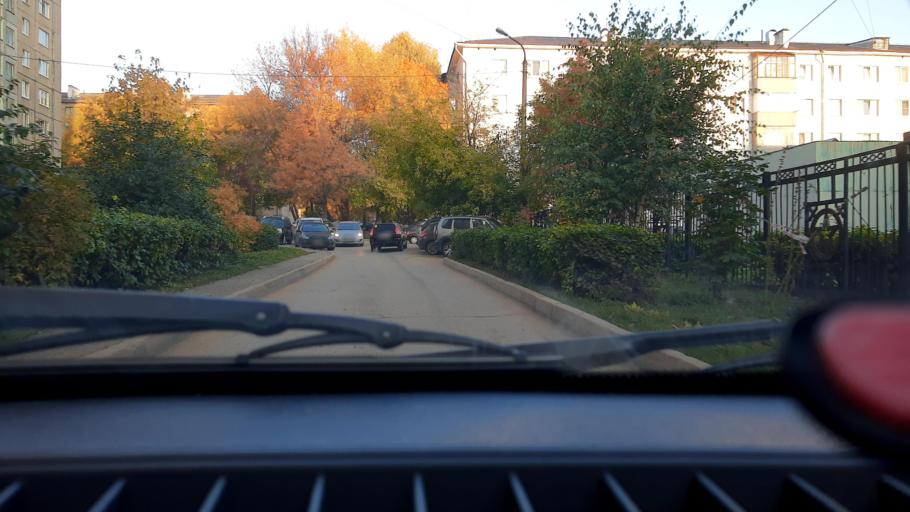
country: RU
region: Bashkortostan
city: Ufa
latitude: 54.7462
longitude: 55.9971
